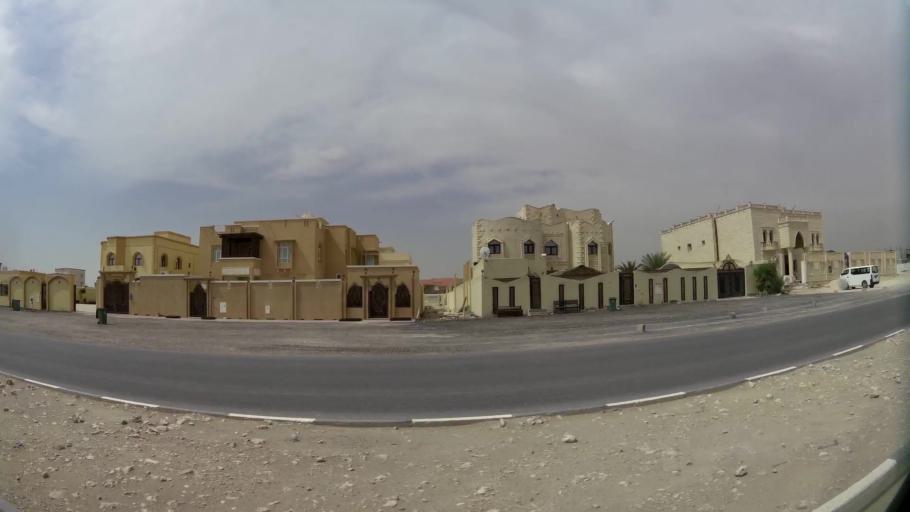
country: QA
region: Baladiyat ad Dawhah
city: Doha
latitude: 25.2167
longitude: 51.4791
